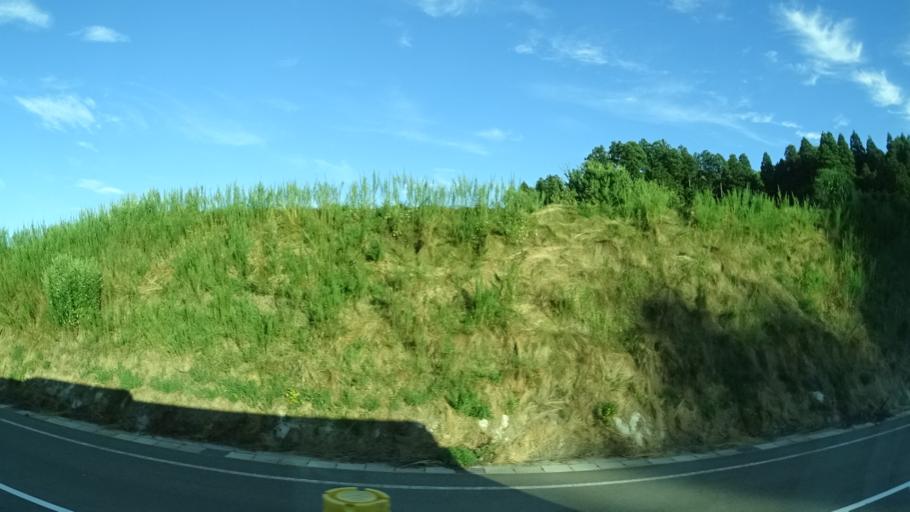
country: JP
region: Ishikawa
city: Nanao
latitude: 37.2938
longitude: 136.8942
